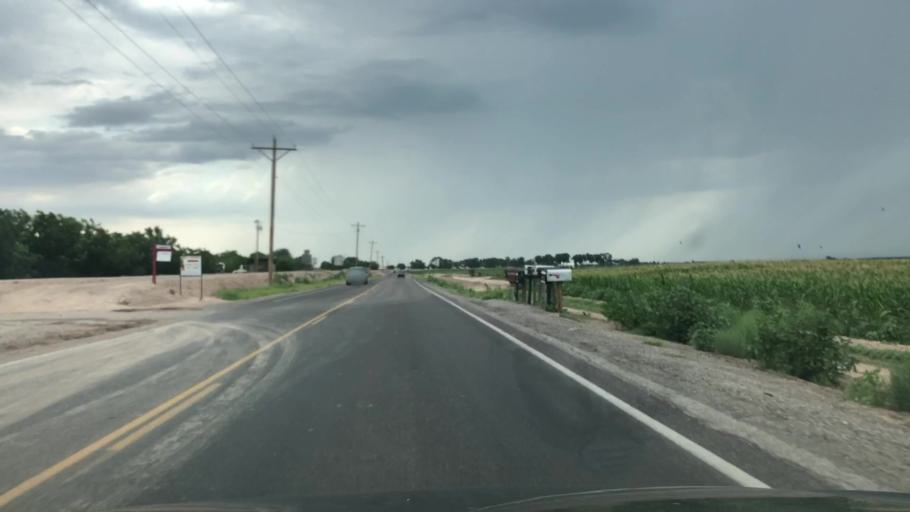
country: US
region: New Mexico
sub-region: Dona Ana County
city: Anthony
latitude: 32.0186
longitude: -106.6689
